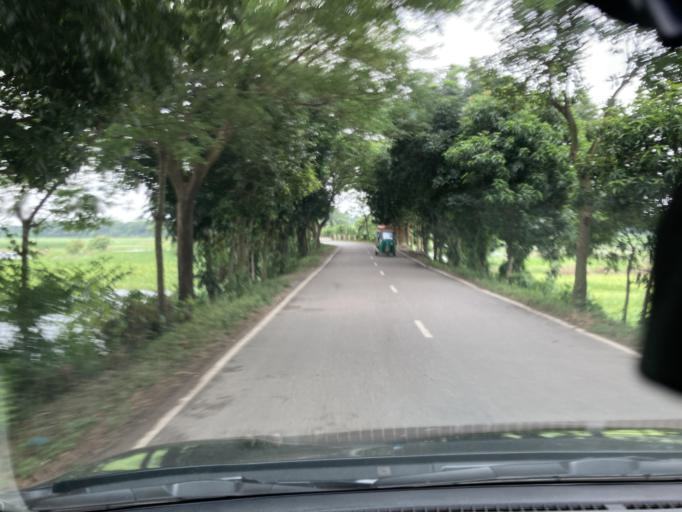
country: BD
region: Dhaka
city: Azimpur
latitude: 23.7775
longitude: 90.2073
